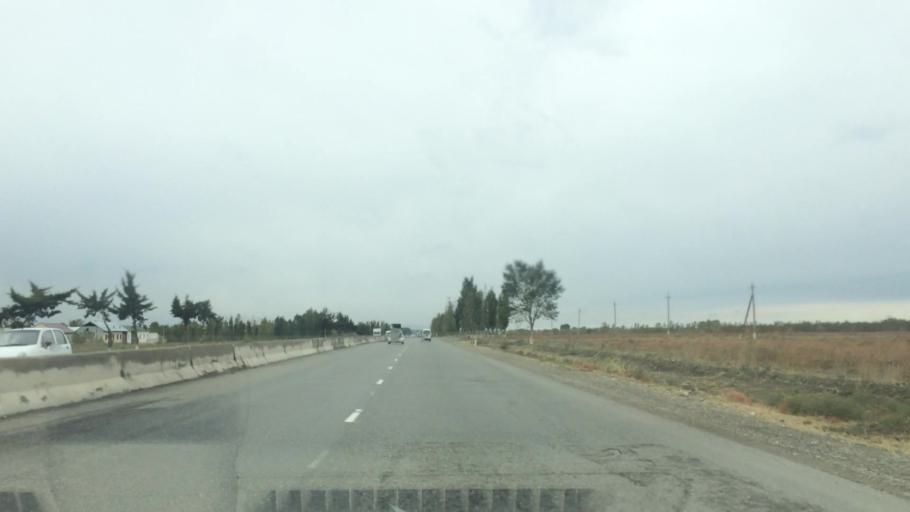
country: UZ
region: Samarqand
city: Bulung'ur
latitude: 39.7897
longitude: 67.3177
